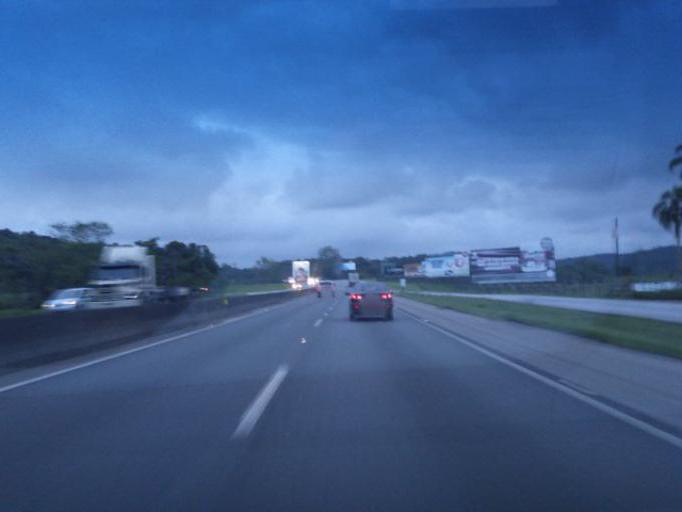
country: BR
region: Santa Catarina
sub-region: Barra Velha
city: Barra Velha
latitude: -26.5701
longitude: -48.7211
